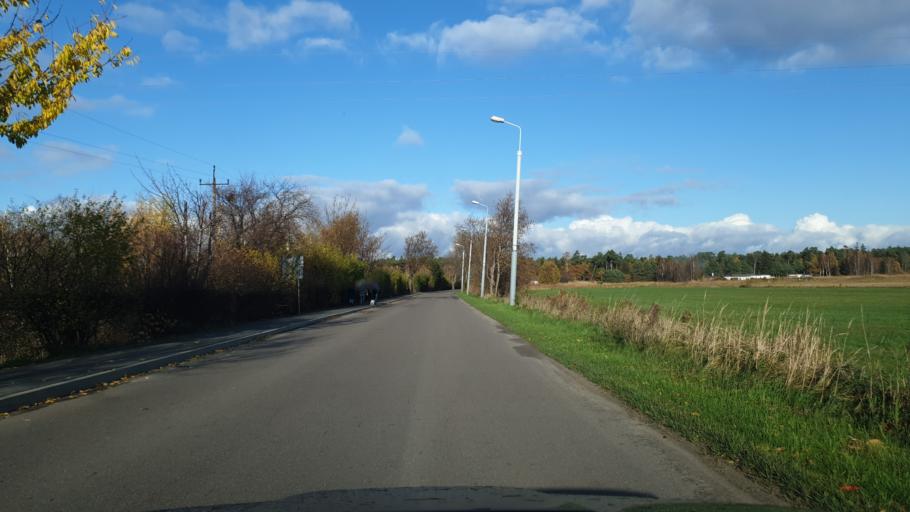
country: PL
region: Pomeranian Voivodeship
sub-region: Powiat pucki
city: Jastrzebia Gora
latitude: 54.8263
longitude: 18.2439
